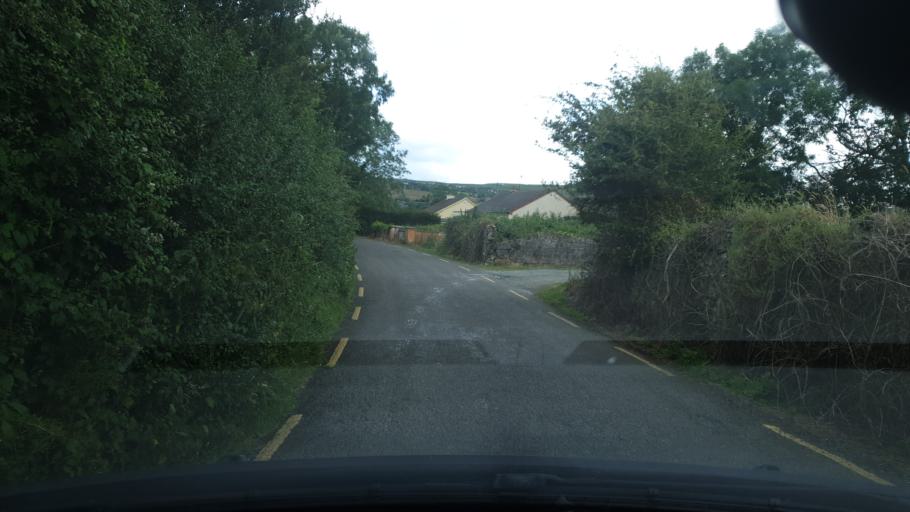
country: IE
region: Munster
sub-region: Ciarrai
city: Tralee
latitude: 52.2510
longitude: -9.6457
